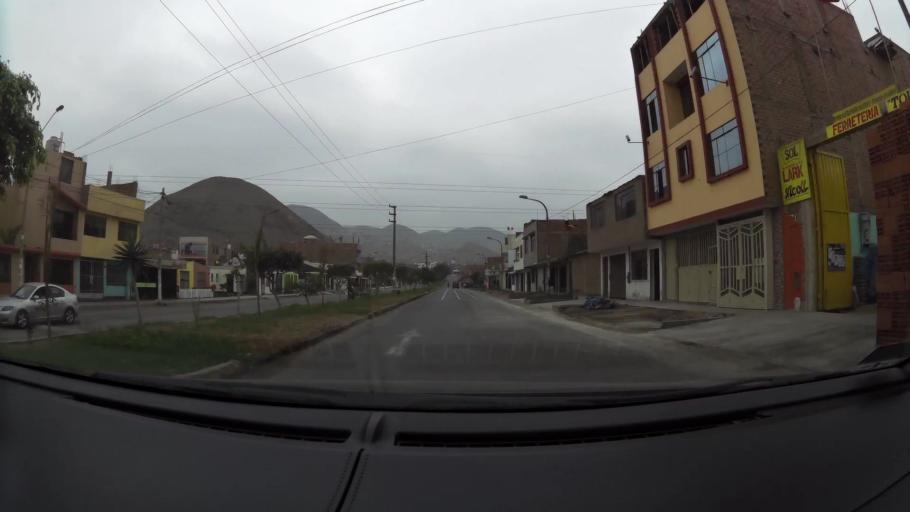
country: PE
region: Lima
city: Ventanilla
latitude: -11.9290
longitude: -77.0795
